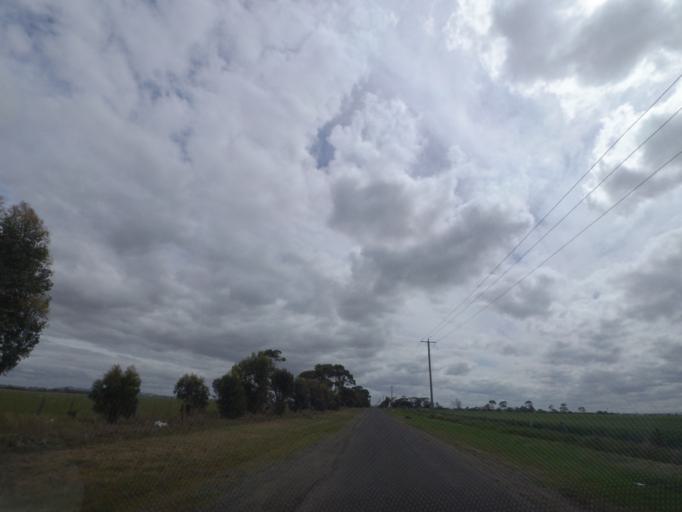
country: AU
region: Victoria
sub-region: Wyndham
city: Tarneit
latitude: -37.8422
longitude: 144.6310
